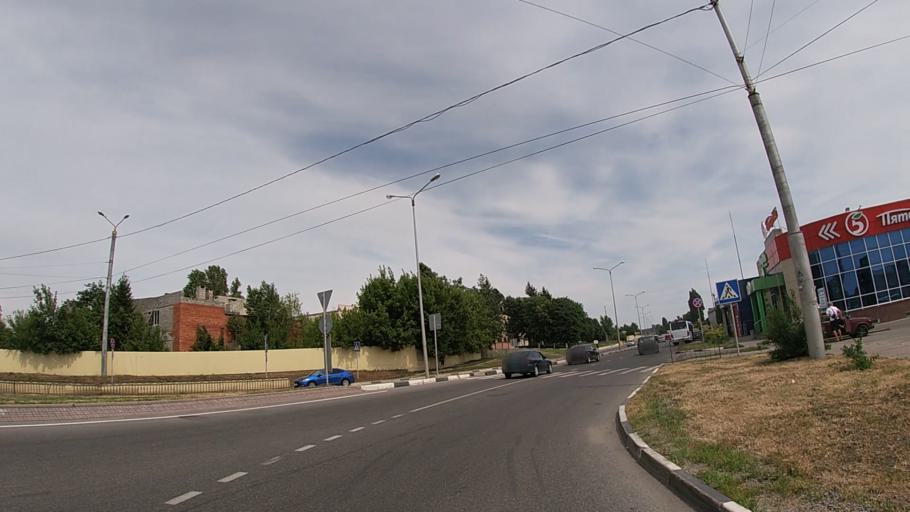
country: RU
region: Belgorod
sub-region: Belgorodskiy Rayon
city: Belgorod
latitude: 50.6132
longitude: 36.5358
